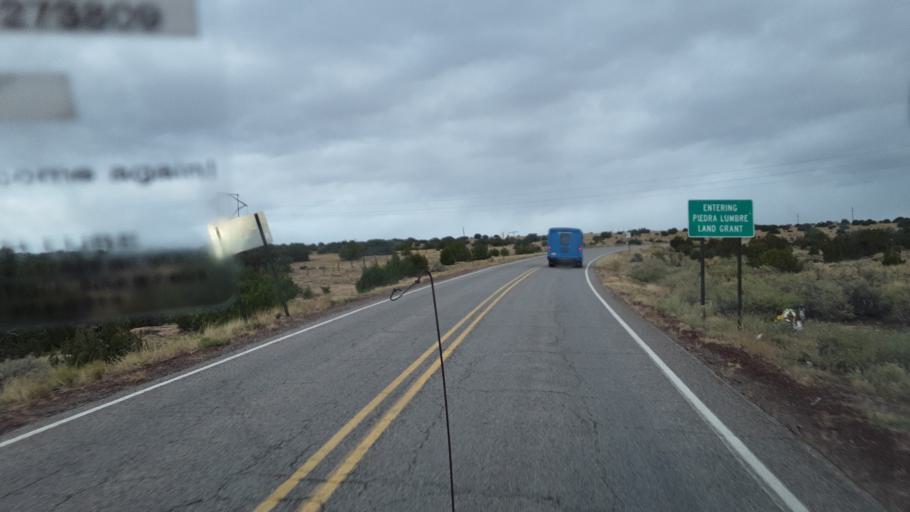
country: US
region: New Mexico
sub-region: Rio Arriba County
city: Santa Teresa
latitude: 36.2436
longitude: -106.4028
